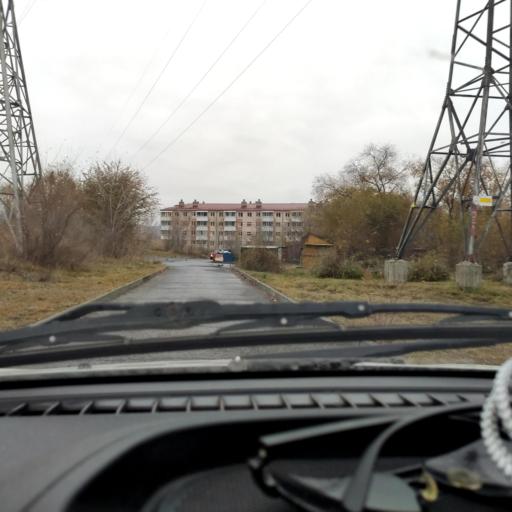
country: RU
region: Samara
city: Zhigulevsk
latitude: 53.4661
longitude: 49.5400
